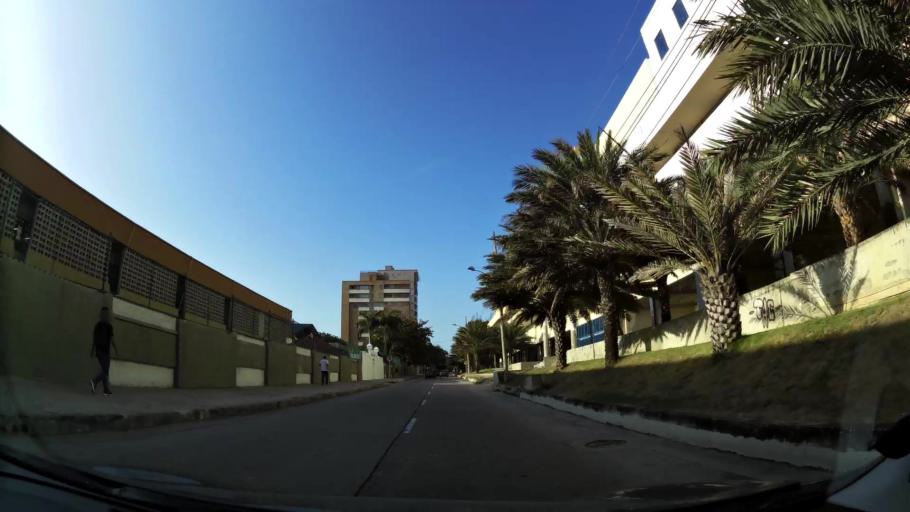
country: CO
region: Atlantico
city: Barranquilla
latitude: 11.0076
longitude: -74.8226
